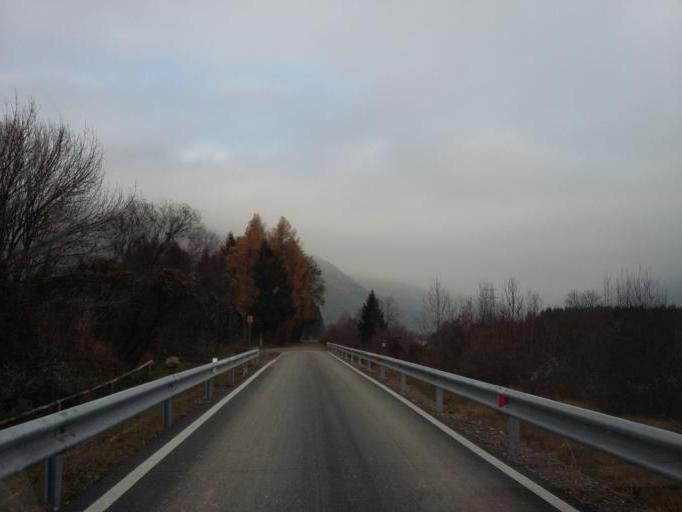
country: IT
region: Trentino-Alto Adige
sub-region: Provincia di Trento
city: Lodrone-Darzo
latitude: 45.8319
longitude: 10.5514
